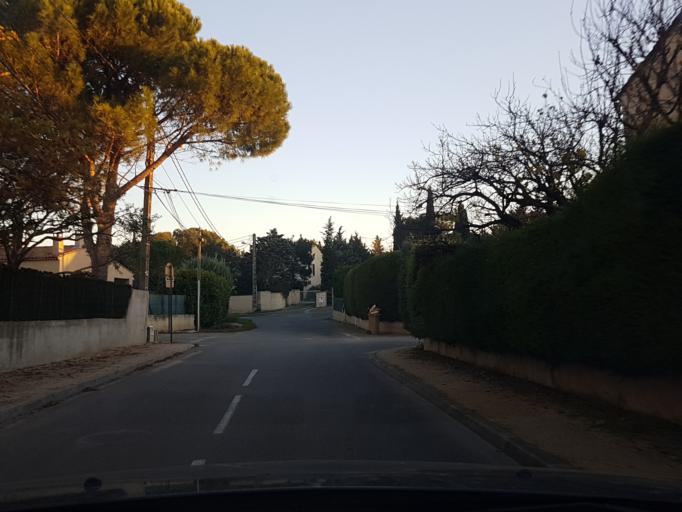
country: FR
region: Provence-Alpes-Cote d'Azur
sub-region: Departement du Vaucluse
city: Vedene
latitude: 43.9669
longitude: 4.9027
